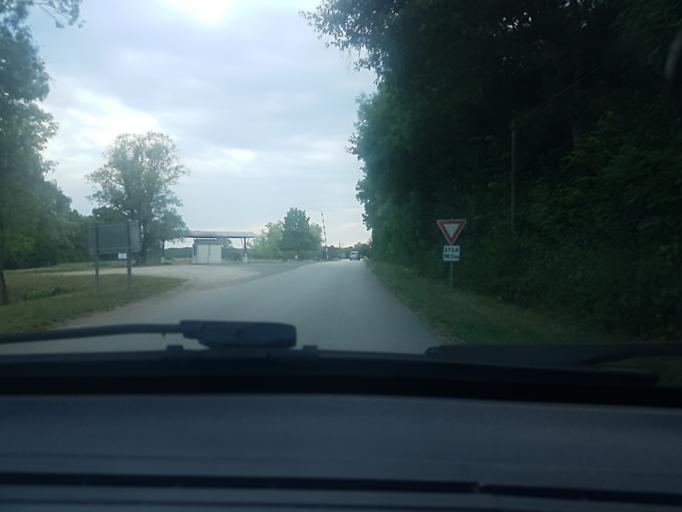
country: FR
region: Bourgogne
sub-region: Departement de Saone-et-Loire
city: Sennecey-le-Grand
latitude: 46.6685
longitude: 4.8227
